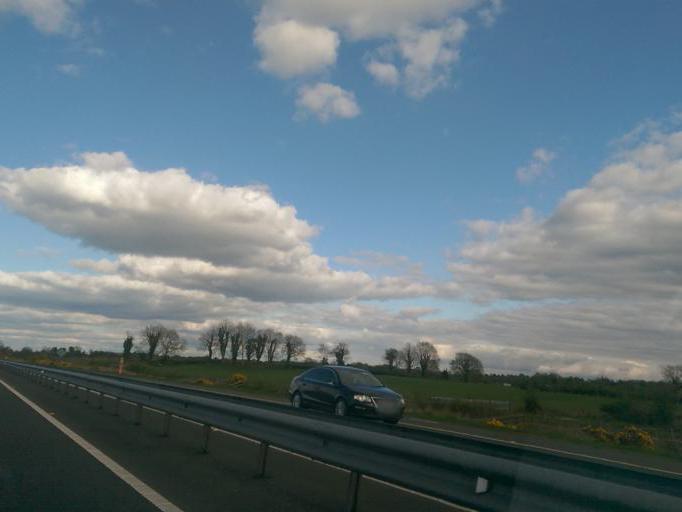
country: IE
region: Leinster
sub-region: An Iarmhi
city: Athlone
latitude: 53.4045
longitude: -8.0333
